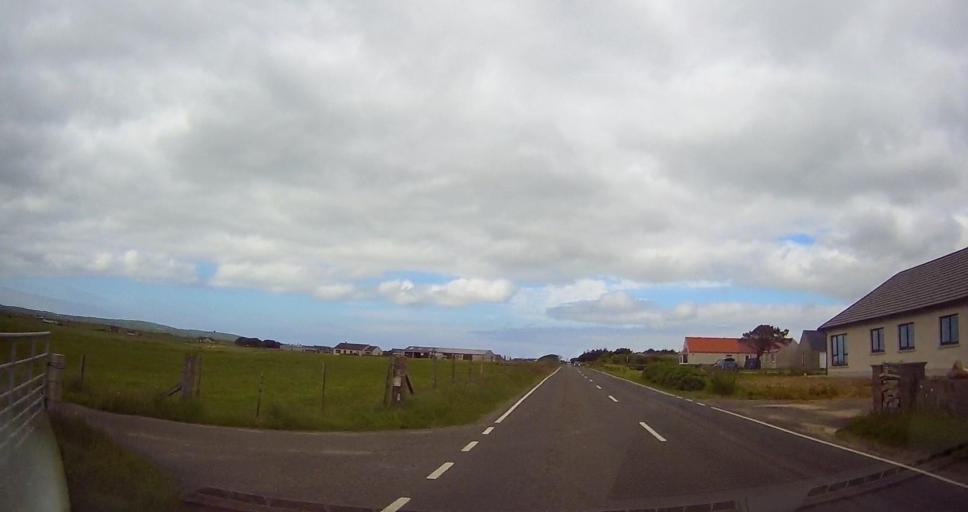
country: GB
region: Scotland
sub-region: Orkney Islands
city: Stromness
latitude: 59.0580
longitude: -3.2184
